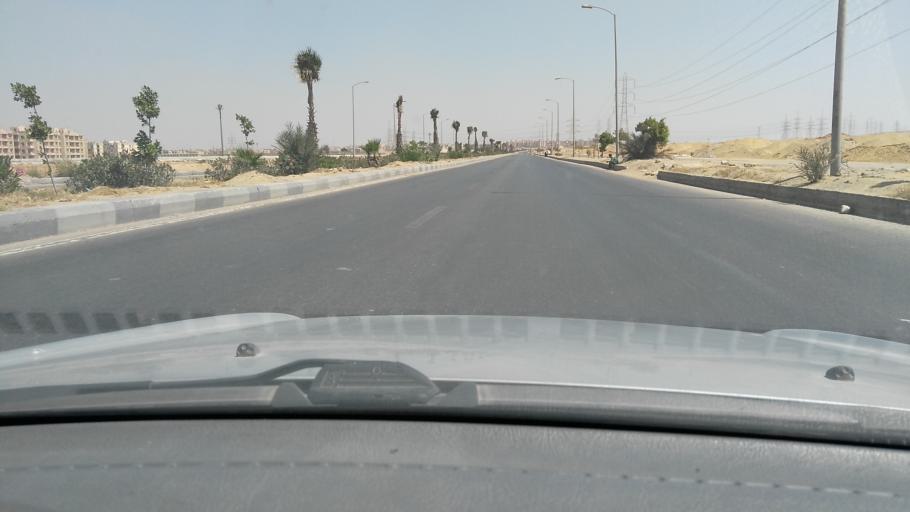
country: EG
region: Al Jizah
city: Madinat Sittah Uktubar
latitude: 29.9378
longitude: 30.9463
